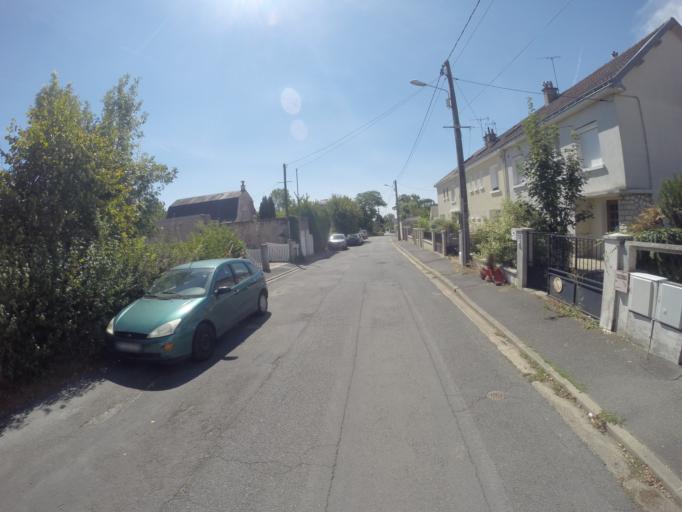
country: FR
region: Centre
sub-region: Departement d'Indre-et-Loire
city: Rochecorbon
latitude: 47.4134
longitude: 0.7133
